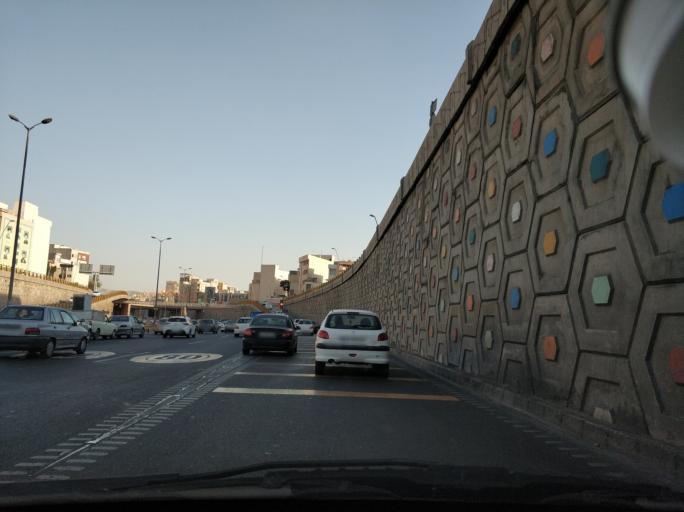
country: IR
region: Tehran
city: Tehran
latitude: 35.6899
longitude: 51.4569
